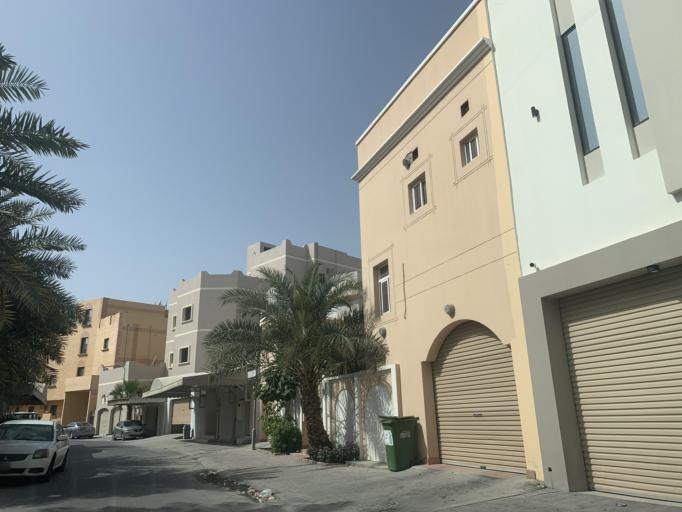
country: BH
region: Northern
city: Ar Rifa'
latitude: 26.1406
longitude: 50.5735
